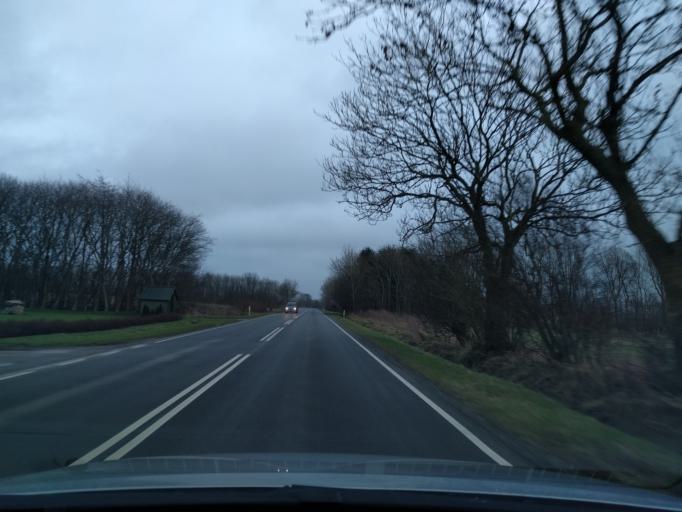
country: DK
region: South Denmark
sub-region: Haderslev Kommune
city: Vojens
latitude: 55.2428
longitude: 9.2132
